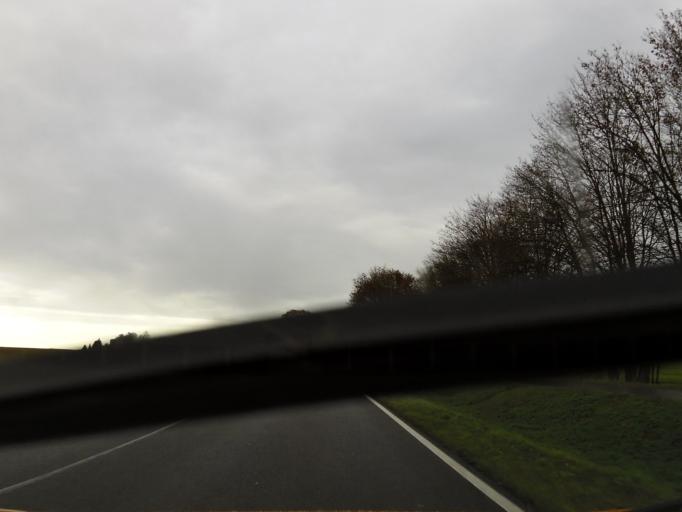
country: DE
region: Saxony-Anhalt
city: Gardelegen
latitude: 52.5687
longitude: 11.3612
